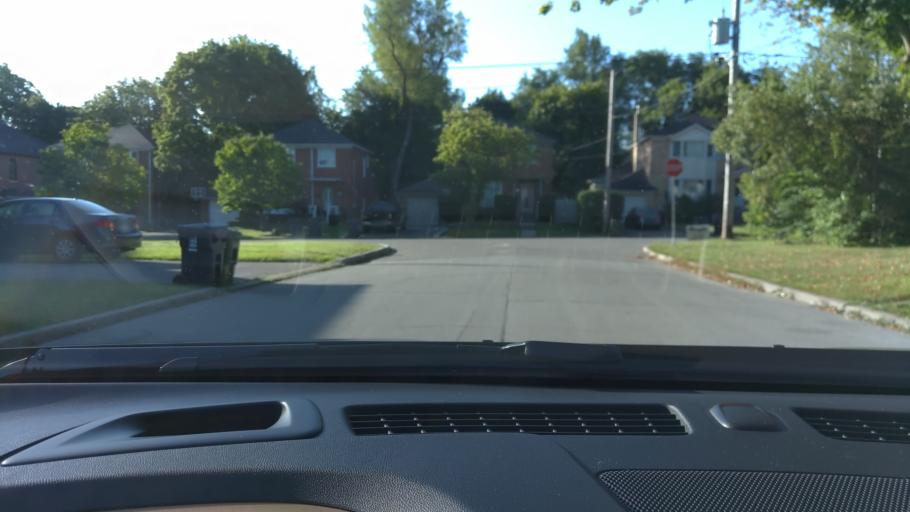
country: CA
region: Ontario
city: Toronto
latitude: 43.7254
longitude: -79.4362
